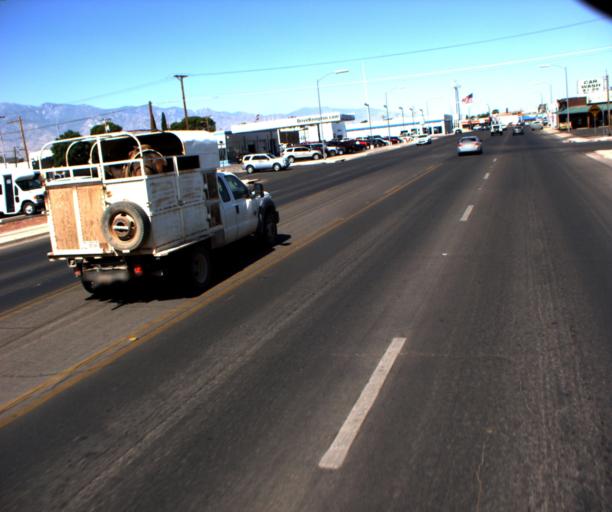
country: US
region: Arizona
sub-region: Graham County
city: Safford
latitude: 32.8344
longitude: -109.7132
